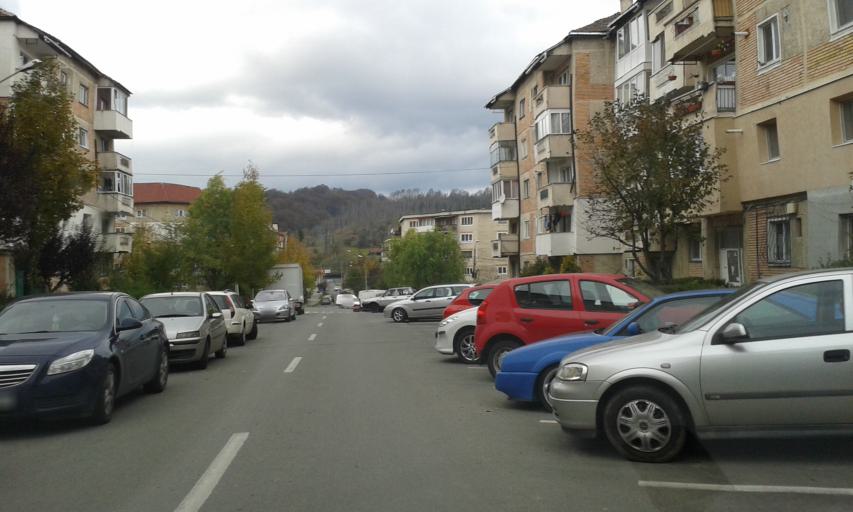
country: RO
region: Hunedoara
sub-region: Municipiul Petrosani
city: Petrosani
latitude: 45.3902
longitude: 23.3769
